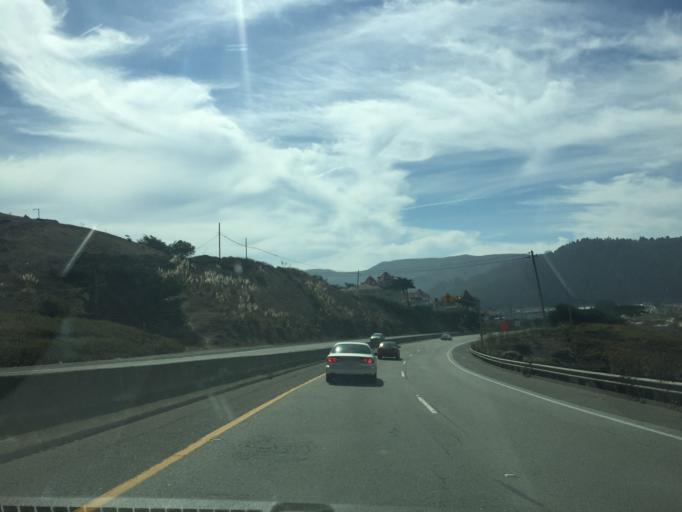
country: US
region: California
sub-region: San Mateo County
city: Pacifica
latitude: 37.6021
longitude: -122.4983
